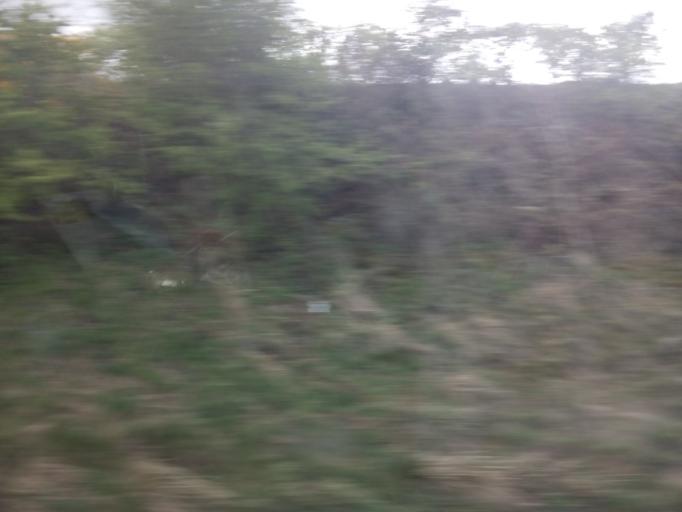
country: GB
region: Scotland
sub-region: The Scottish Borders
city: Chirnside
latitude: 55.8433
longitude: -2.1674
